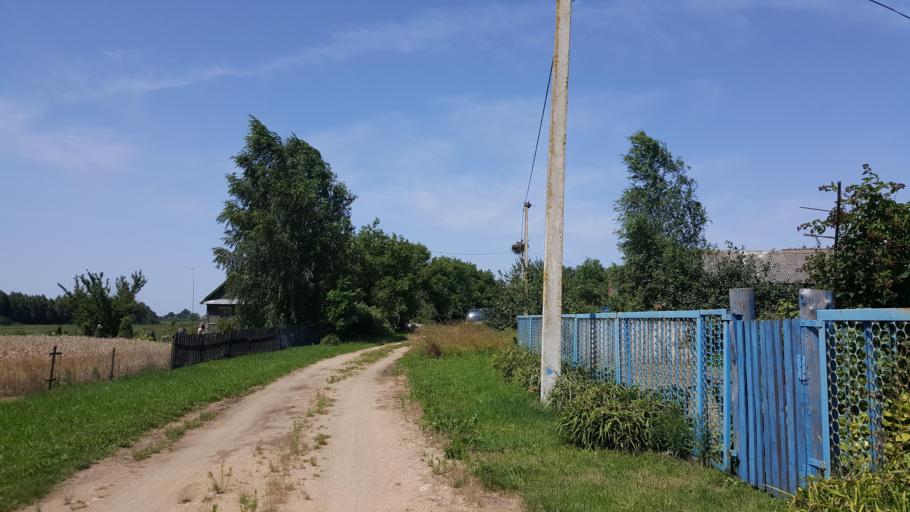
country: BY
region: Brest
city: Vysokaye
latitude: 52.3643
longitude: 23.5256
